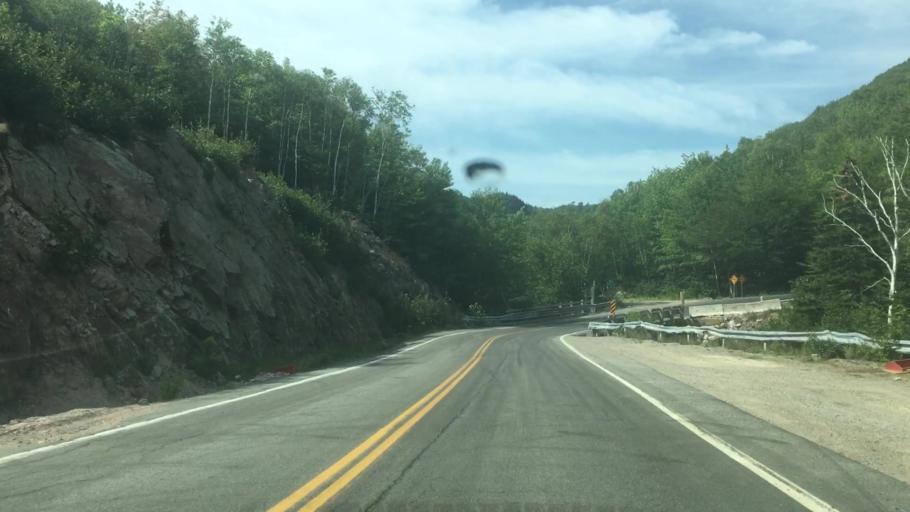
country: CA
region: Nova Scotia
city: Sydney Mines
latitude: 46.5831
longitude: -60.3956
